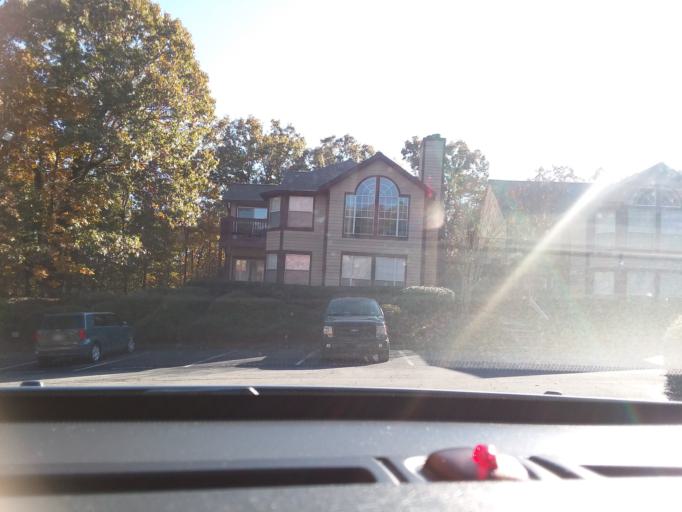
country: US
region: Georgia
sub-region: Gwinnett County
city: Norcross
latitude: 33.9894
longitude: -84.2687
